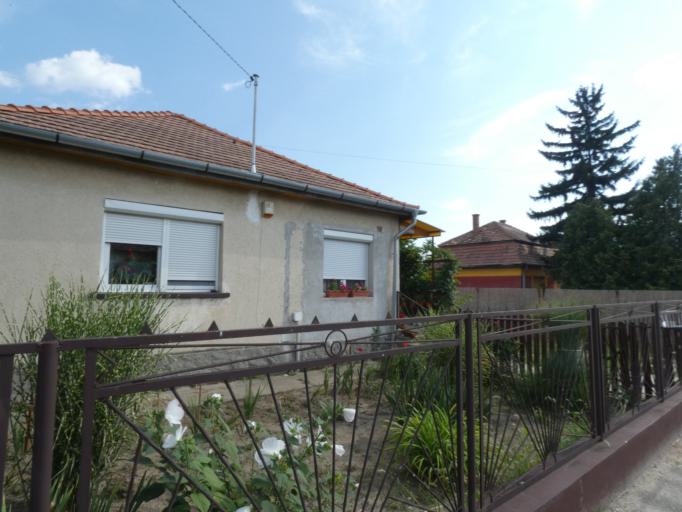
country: HU
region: Pest
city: Taborfalva
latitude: 47.1014
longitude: 19.4807
